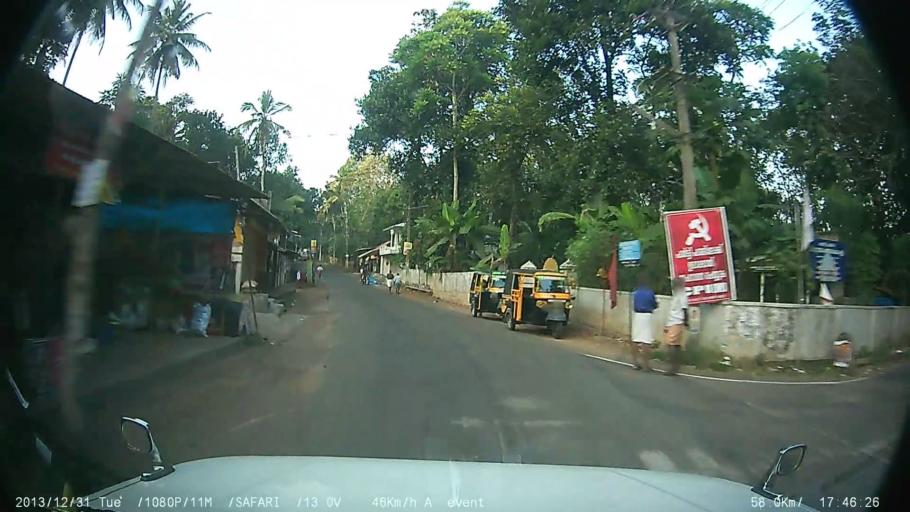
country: IN
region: Kerala
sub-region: Kottayam
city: Vaikam
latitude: 9.7362
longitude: 76.4793
